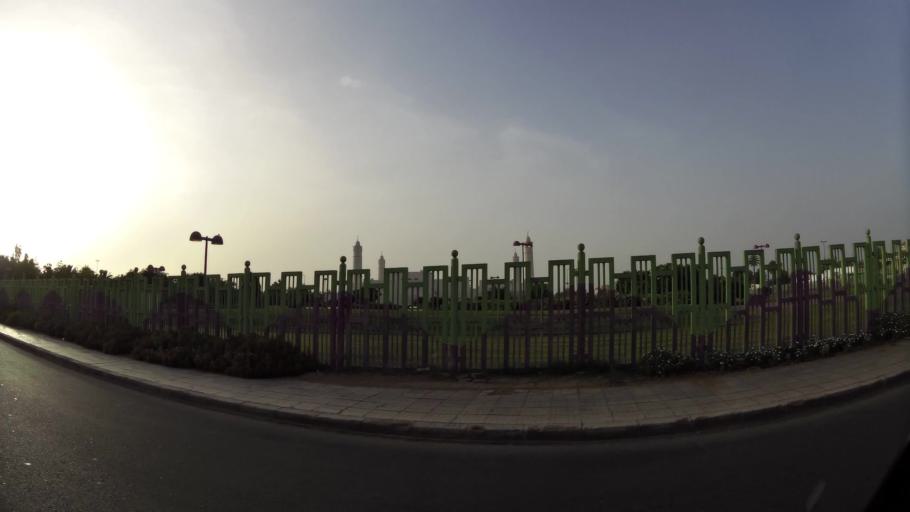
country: OM
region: Al Buraimi
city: Al Buraymi
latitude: 24.2430
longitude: 55.7408
